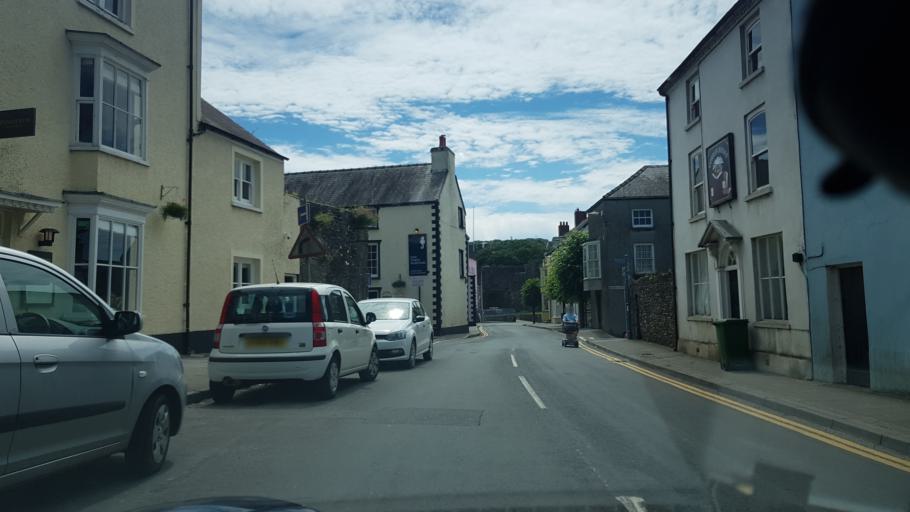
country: GB
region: Wales
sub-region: Carmarthenshire
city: Saint Clears
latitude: 51.7712
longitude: -4.4624
